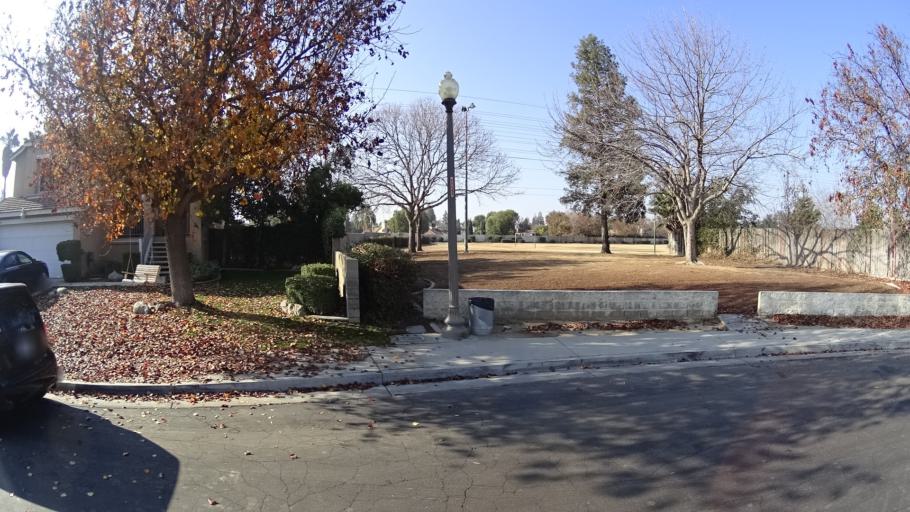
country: US
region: California
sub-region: Kern County
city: Greenacres
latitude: 35.3234
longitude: -119.0958
